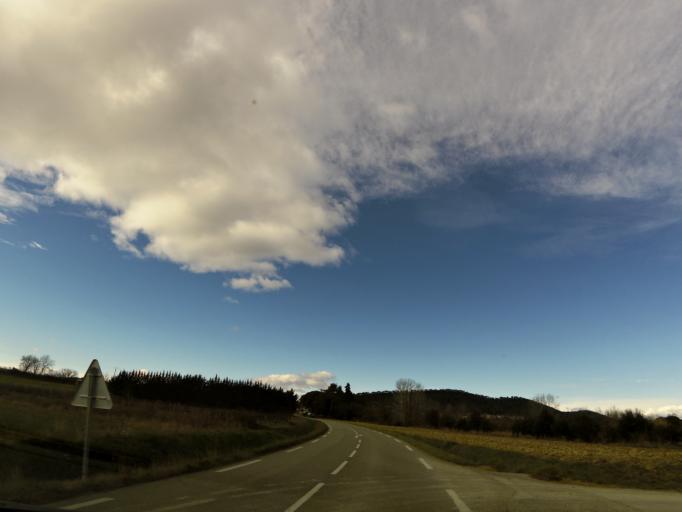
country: FR
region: Languedoc-Roussillon
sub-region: Departement du Gard
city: Sommieres
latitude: 43.8330
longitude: 4.0388
